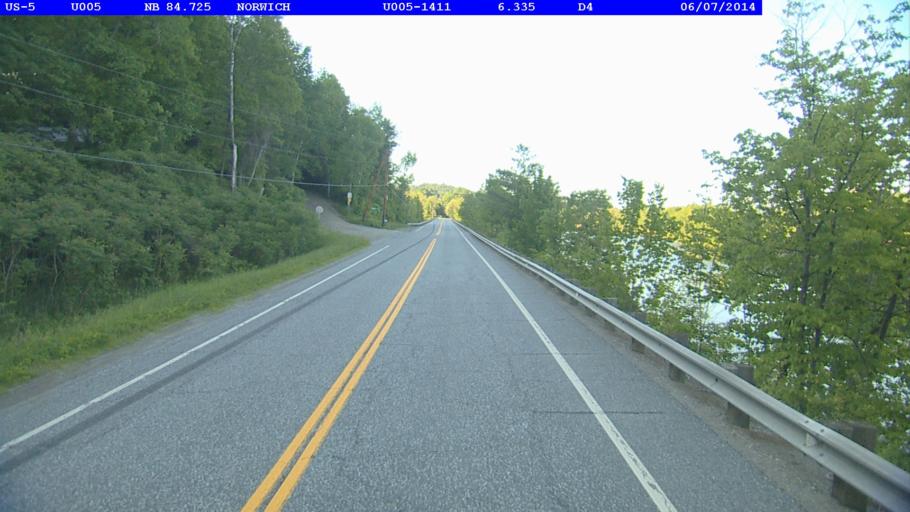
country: US
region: New Hampshire
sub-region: Grafton County
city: Hanover
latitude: 43.7513
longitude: -72.2311
